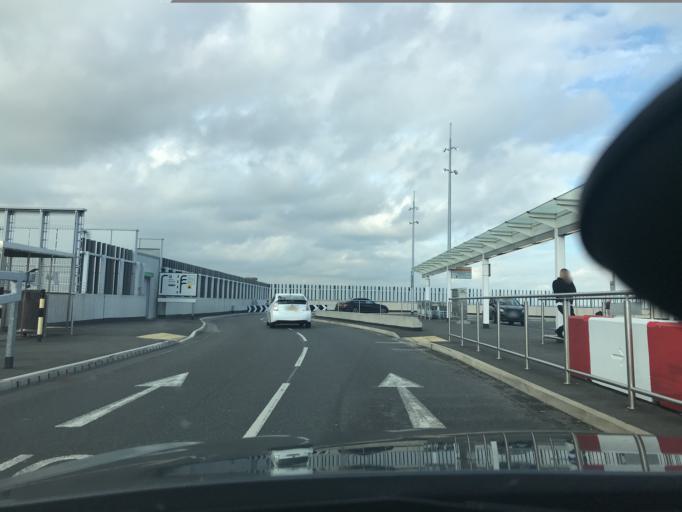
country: GB
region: England
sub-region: Greater London
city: West Drayton
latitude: 51.4695
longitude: -0.4528
